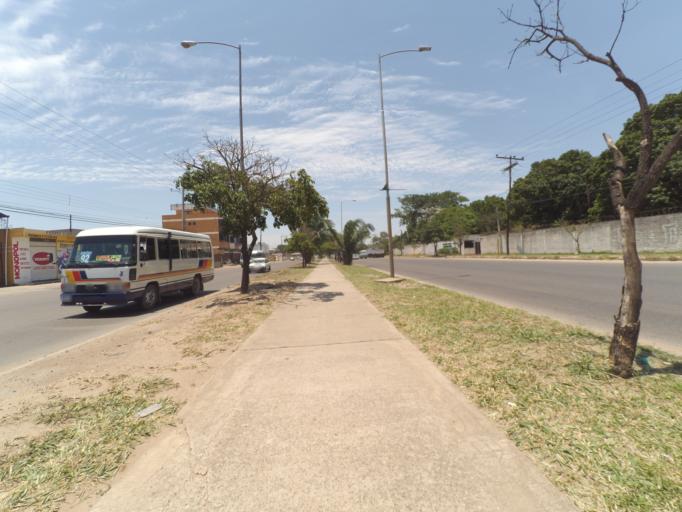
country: BO
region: Santa Cruz
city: Santa Cruz de la Sierra
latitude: -17.8389
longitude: -63.2390
